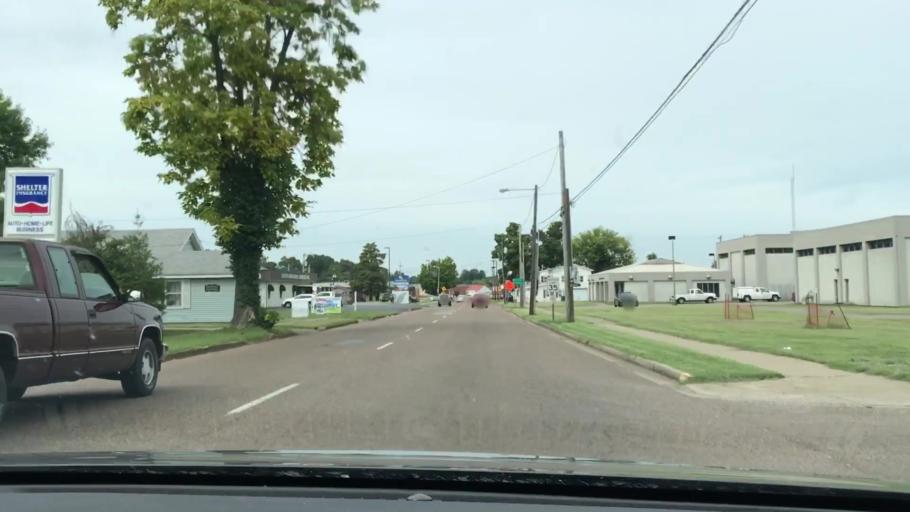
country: US
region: Kentucky
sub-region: Marshall County
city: Benton
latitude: 36.8613
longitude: -88.3500
